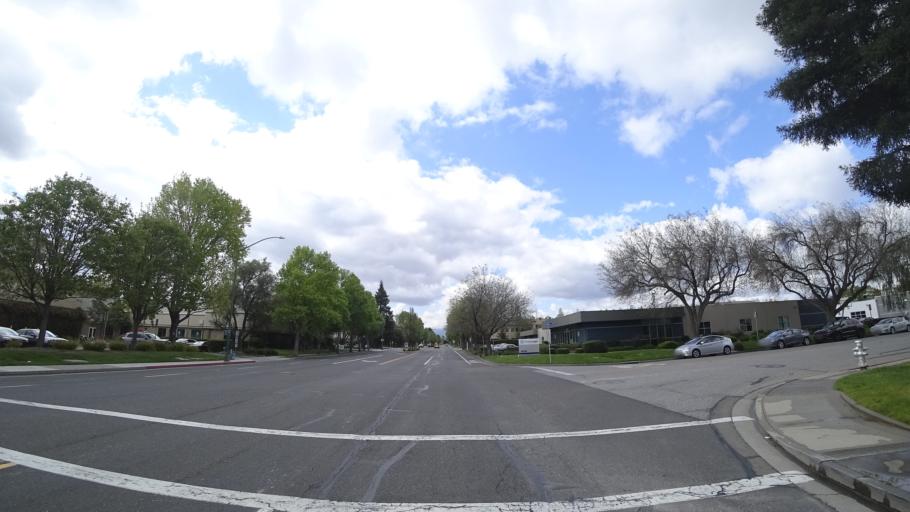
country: US
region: California
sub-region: Santa Clara County
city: Mountain View
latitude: 37.4012
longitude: -122.0519
